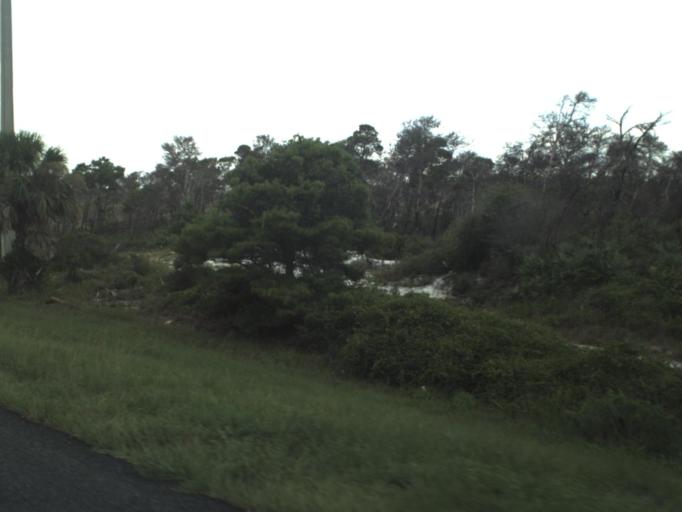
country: US
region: Florida
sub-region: Martin County
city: Hobe Sound
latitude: 27.0289
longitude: -80.1103
